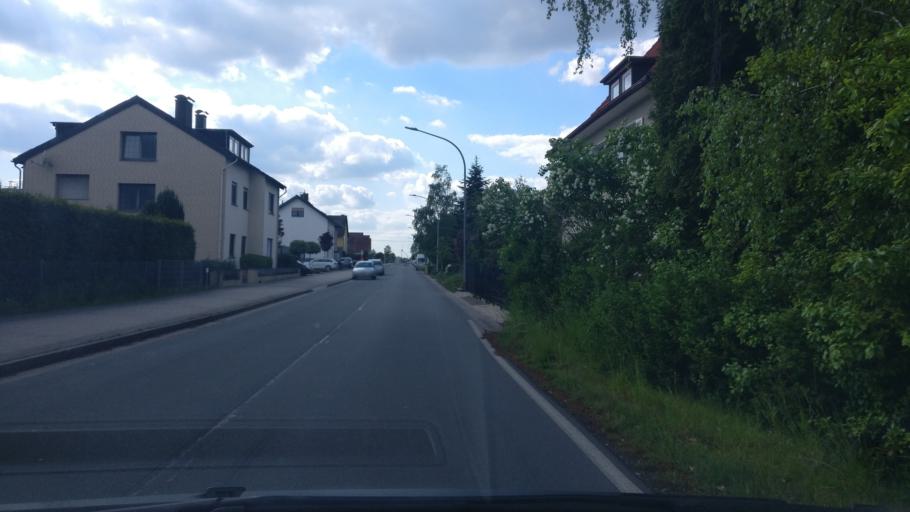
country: DE
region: North Rhine-Westphalia
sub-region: Regierungsbezirk Detmold
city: Leopoldshohe
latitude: 52.0077
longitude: 8.7052
